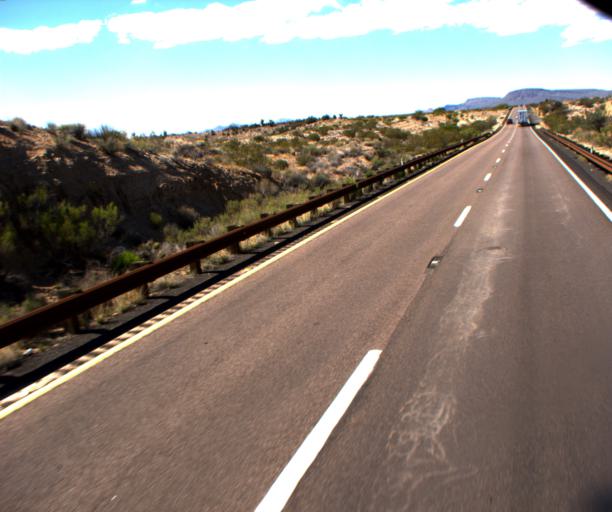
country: US
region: Arizona
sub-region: Mohave County
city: Kingman
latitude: 35.0935
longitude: -113.6656
